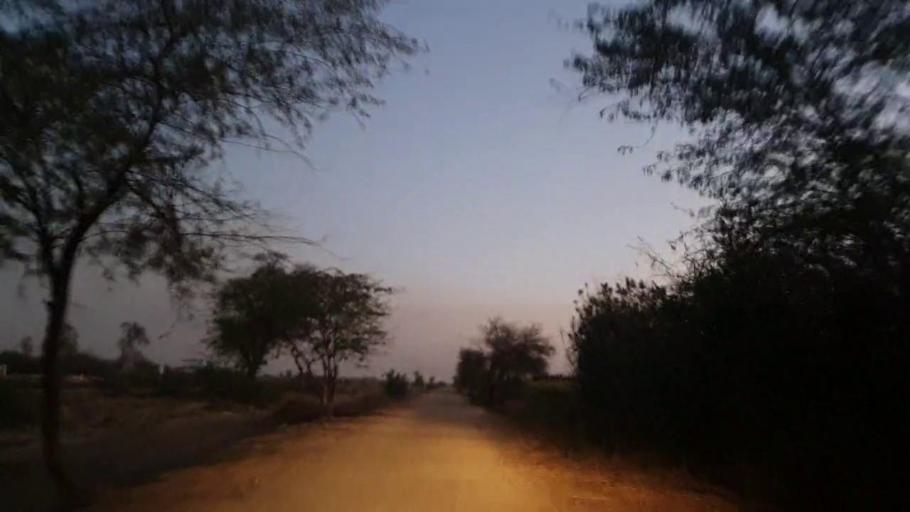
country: PK
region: Sindh
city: Nawabshah
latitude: 26.3406
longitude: 68.3710
